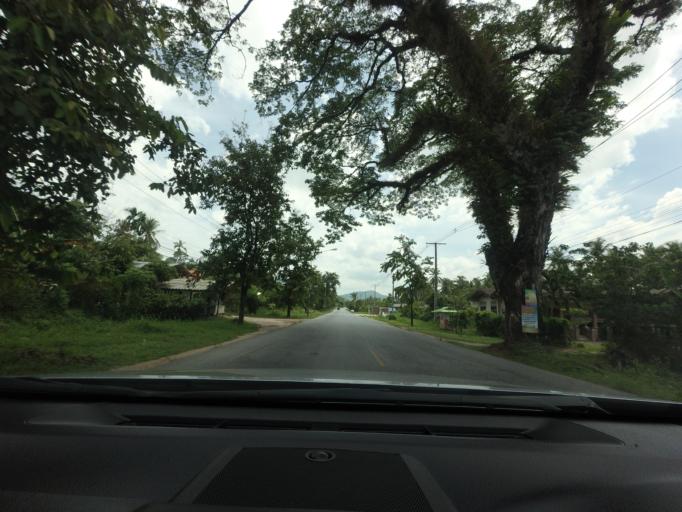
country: TH
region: Yala
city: Raman
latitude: 6.4646
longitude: 101.3815
